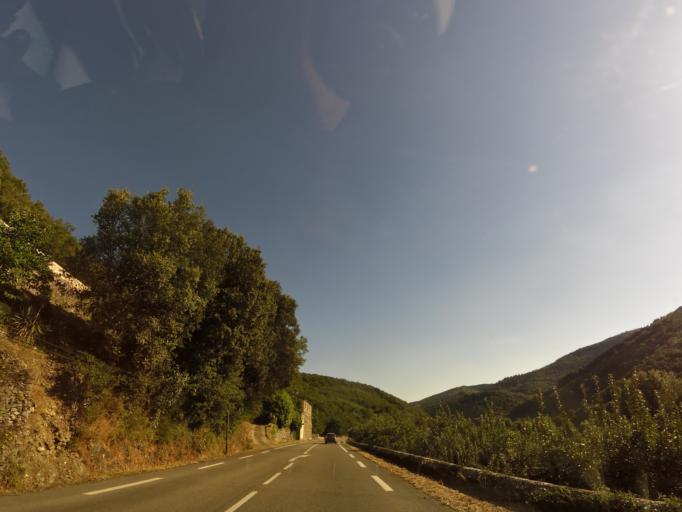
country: FR
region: Languedoc-Roussillon
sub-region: Departement du Gard
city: Sumene
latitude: 43.9901
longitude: 3.6884
